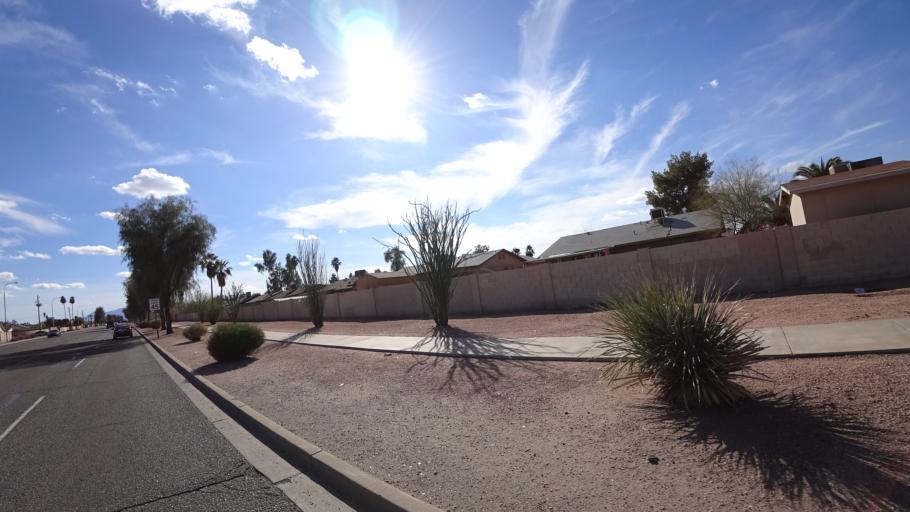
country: US
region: Arizona
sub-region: Maricopa County
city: Glendale
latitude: 33.5045
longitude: -112.2206
